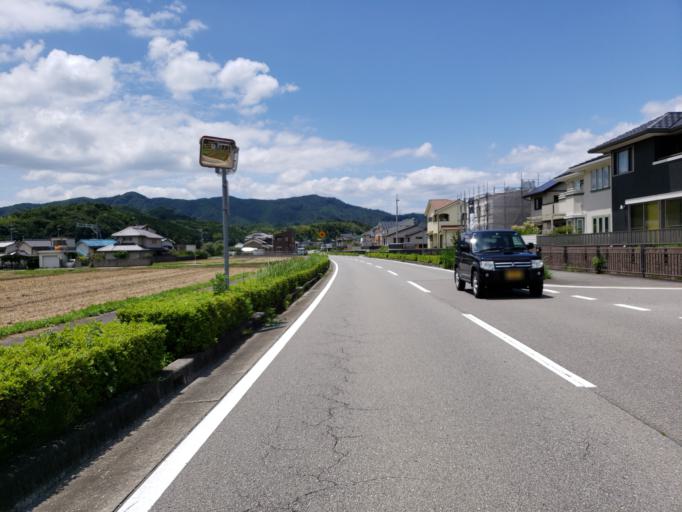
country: JP
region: Hyogo
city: Himeji
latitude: 34.9283
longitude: 134.7364
